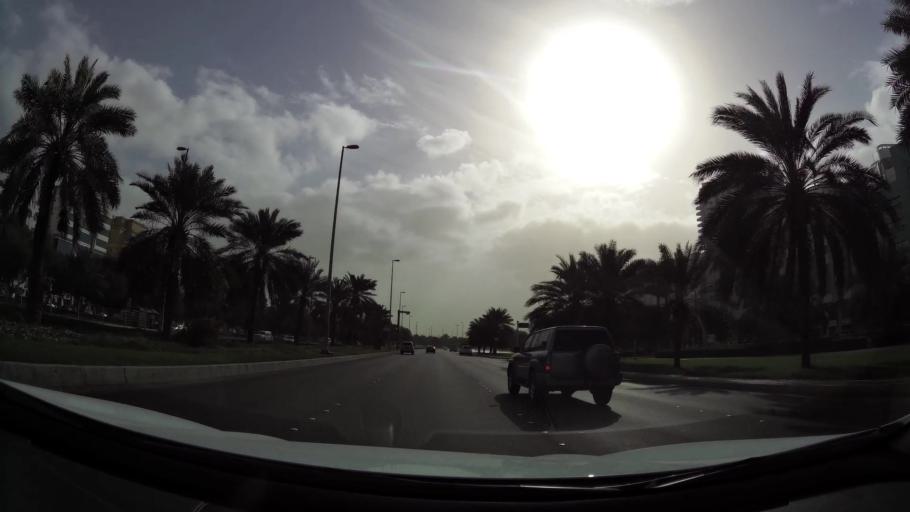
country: AE
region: Abu Dhabi
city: Abu Dhabi
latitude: 24.4330
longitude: 54.4361
